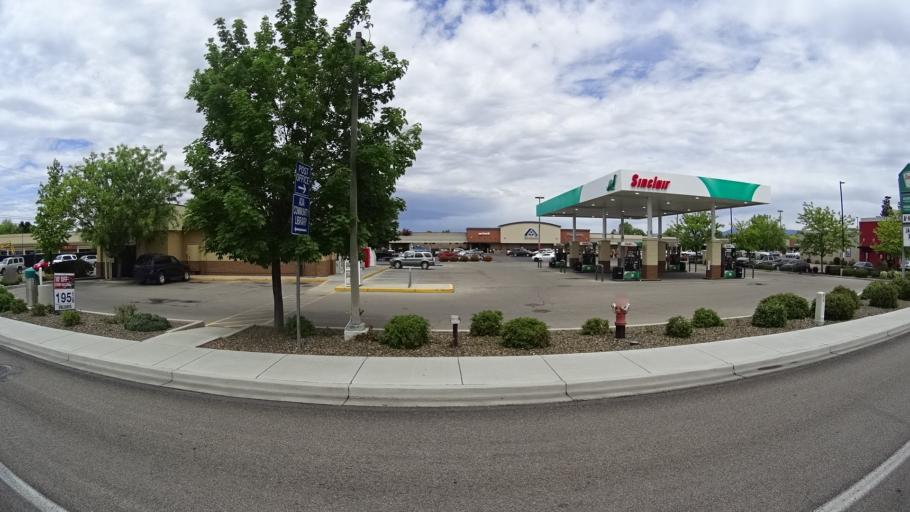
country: US
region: Idaho
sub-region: Ada County
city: Meridian
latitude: 43.5904
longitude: -116.3137
